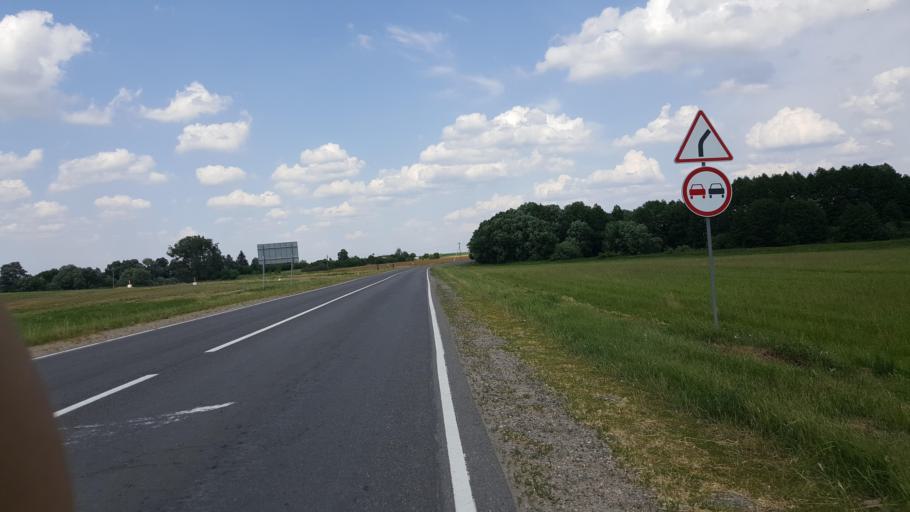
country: BY
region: Brest
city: Kamyanyets
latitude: 52.4020
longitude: 23.7843
